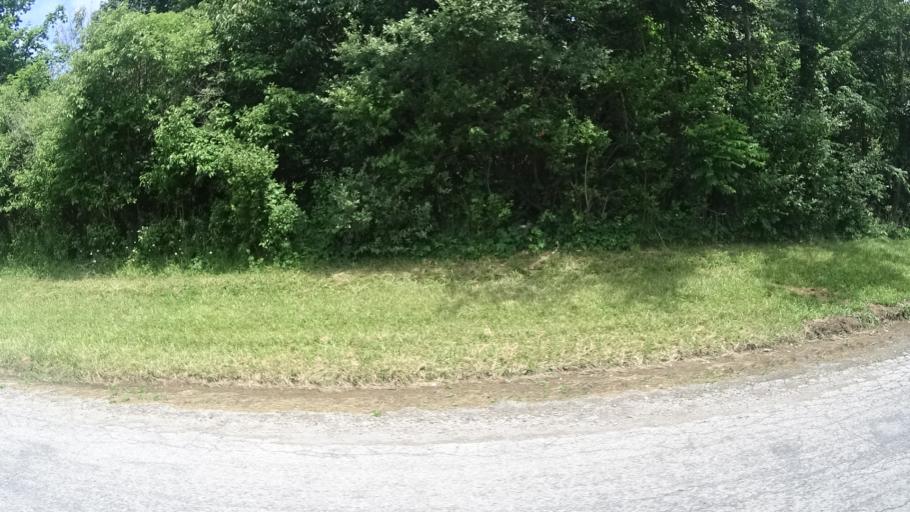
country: US
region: Ohio
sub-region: Huron County
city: Wakeman
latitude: 41.2986
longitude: -82.3512
